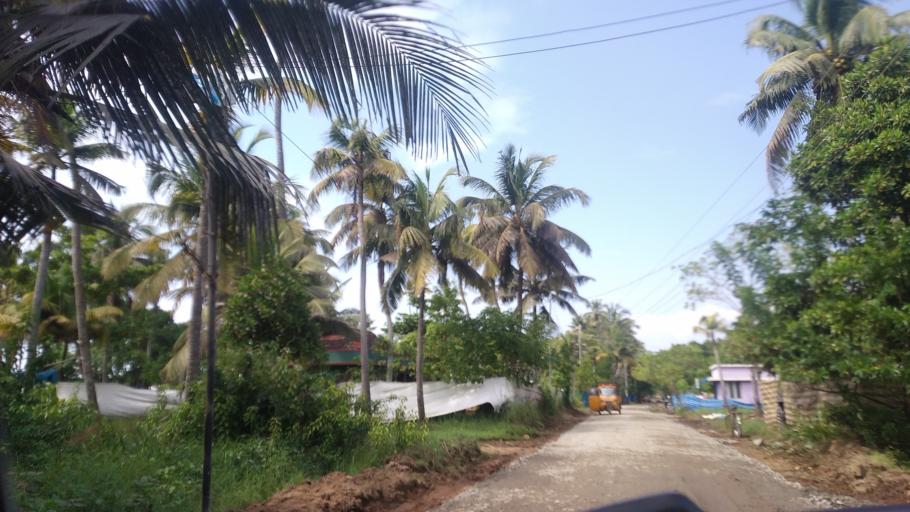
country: IN
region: Kerala
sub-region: Ernakulam
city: Elur
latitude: 10.0557
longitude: 76.2020
